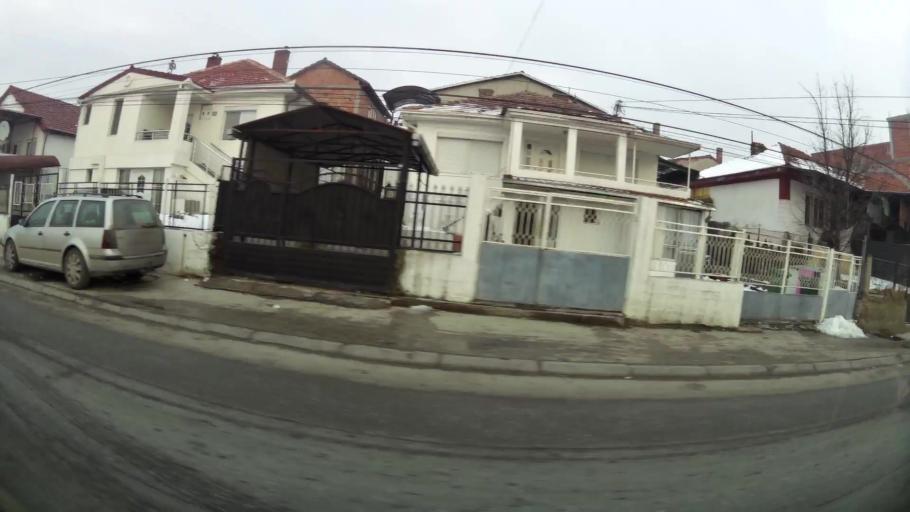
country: MK
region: Suto Orizari
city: Suto Orizare
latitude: 42.0359
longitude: 21.4261
